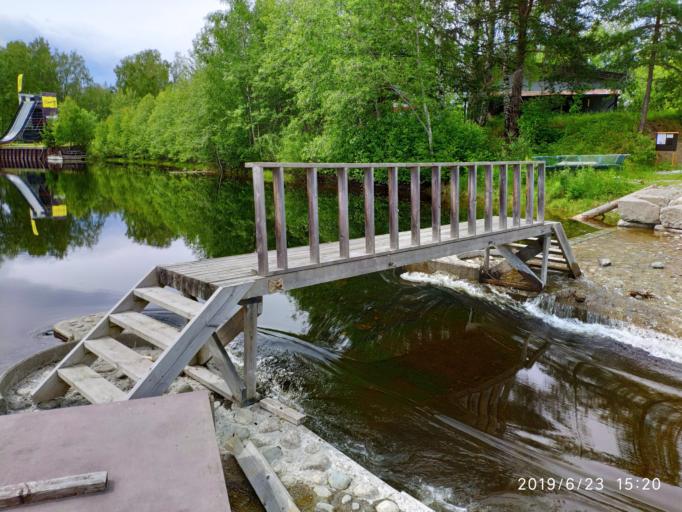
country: NO
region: Buskerud
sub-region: Ringerike
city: Honefoss
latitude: 60.1932
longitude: 10.3026
